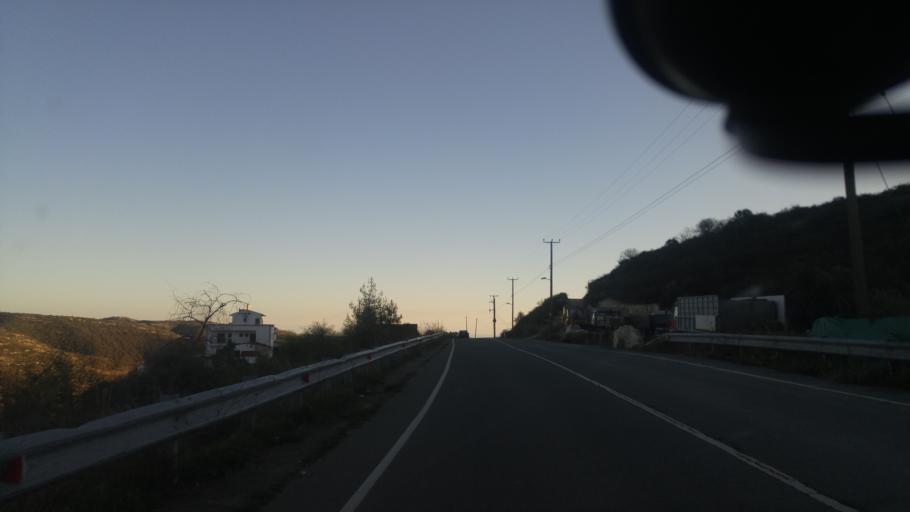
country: CY
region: Limassol
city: Pachna
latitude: 34.8395
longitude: 32.8084
